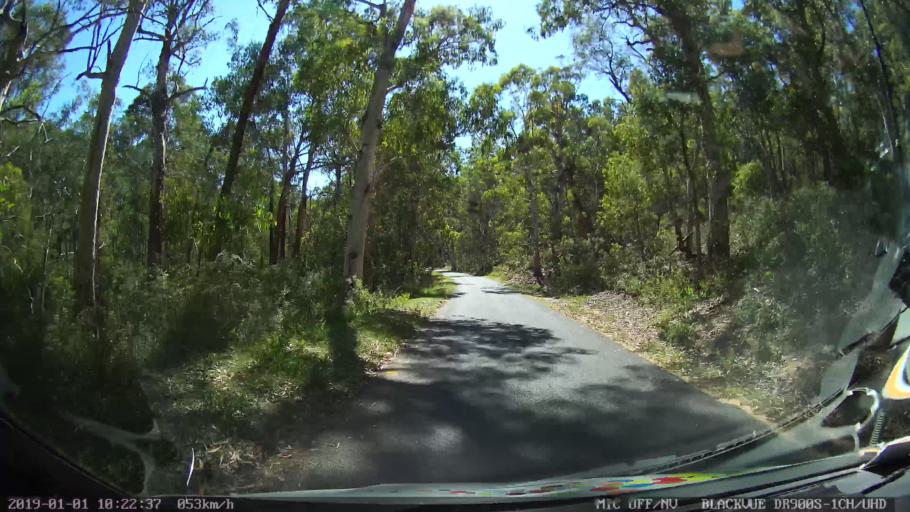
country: AU
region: New South Wales
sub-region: Snowy River
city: Jindabyne
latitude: -36.0774
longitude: 148.2054
